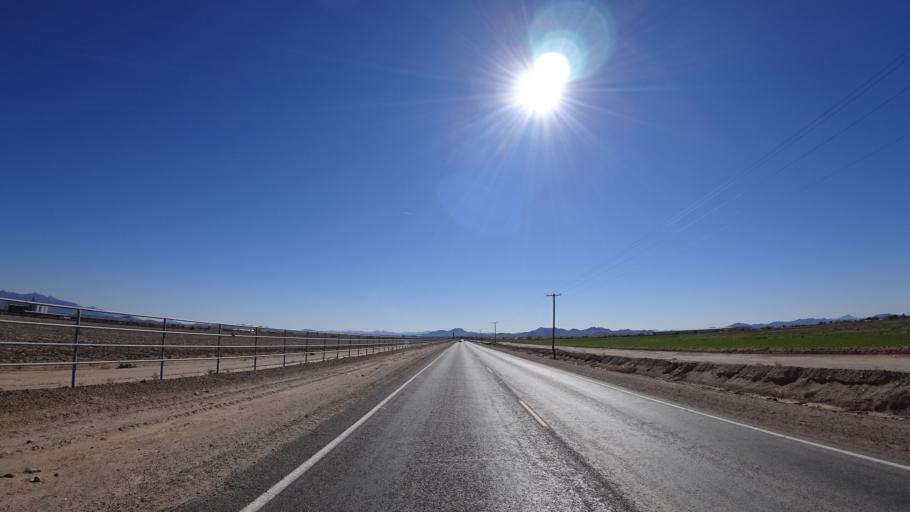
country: US
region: Arizona
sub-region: Maricopa County
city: Buckeye
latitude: 33.3992
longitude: -112.5215
